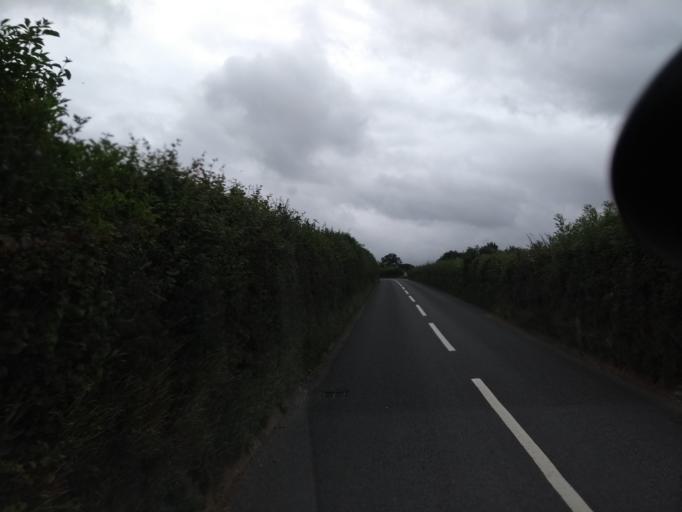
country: GB
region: England
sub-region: Somerset
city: Stoke-sub-Hamdon
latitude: 50.9337
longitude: -2.7655
